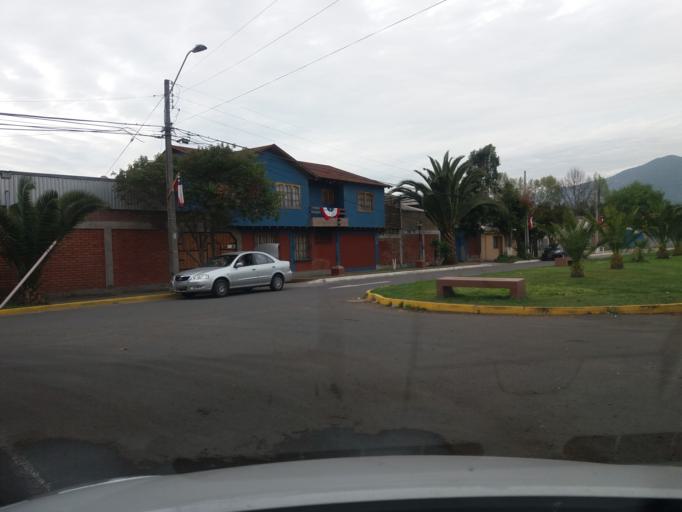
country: CL
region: Valparaiso
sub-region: Provincia de Quillota
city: Hacienda La Calera
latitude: -32.7780
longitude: -71.1841
